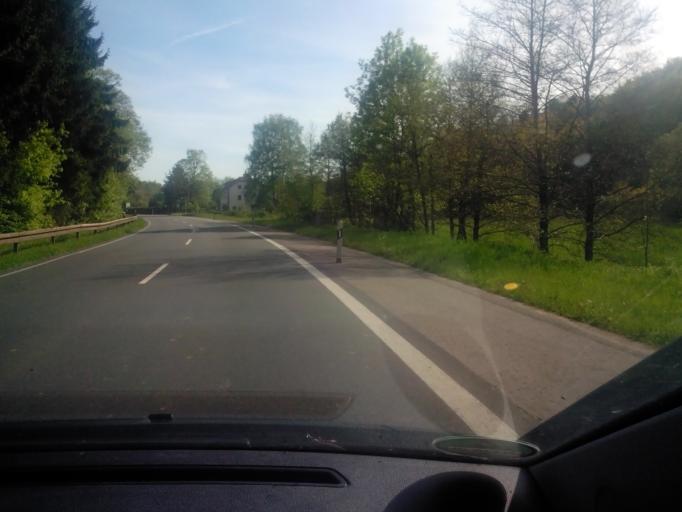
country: DE
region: Saarland
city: Schmelz
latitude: 49.4073
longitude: 6.8477
